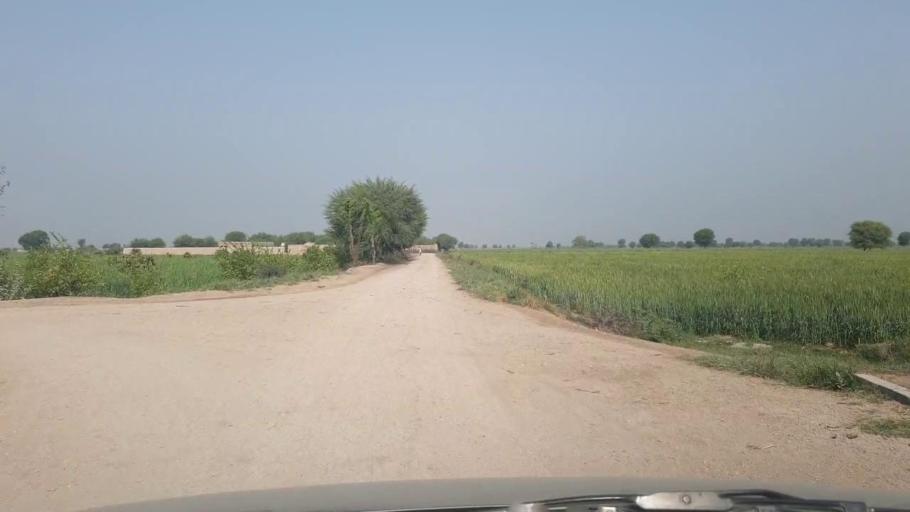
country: PK
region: Sindh
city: Umarkot
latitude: 25.4065
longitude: 69.7191
